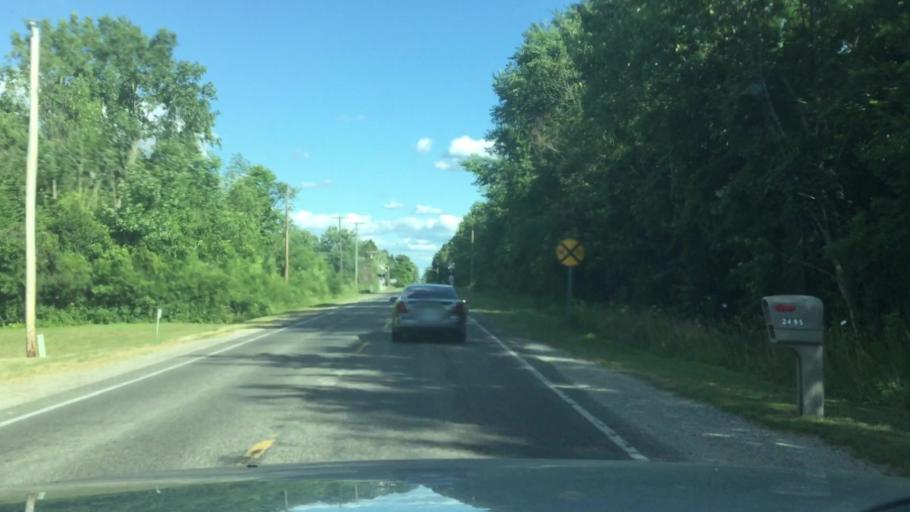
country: US
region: Michigan
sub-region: Saginaw County
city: Saginaw
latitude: 43.3857
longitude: -83.9271
